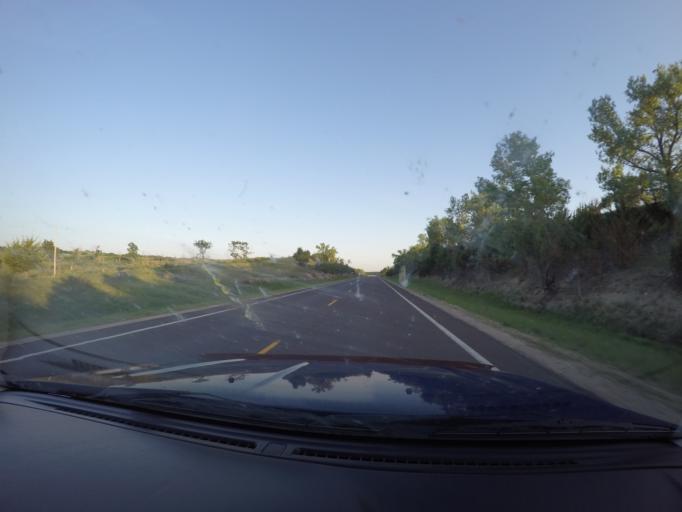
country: US
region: Kansas
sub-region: Marshall County
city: Blue Rapids
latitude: 39.4828
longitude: -96.7549
